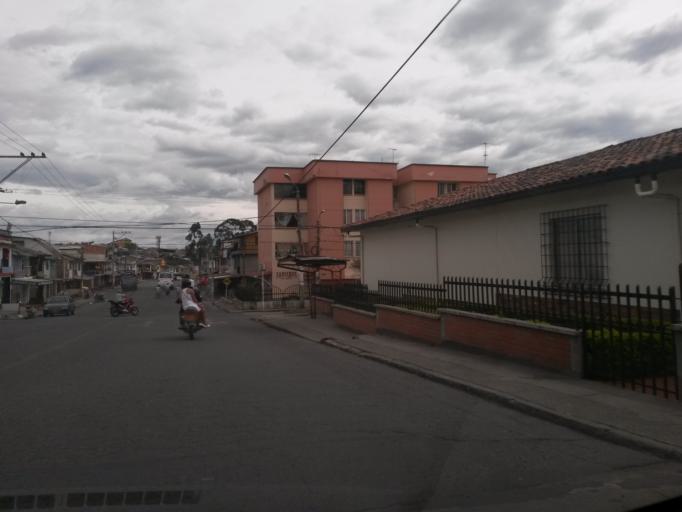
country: CO
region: Cauca
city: Popayan
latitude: 2.4464
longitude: -76.6207
